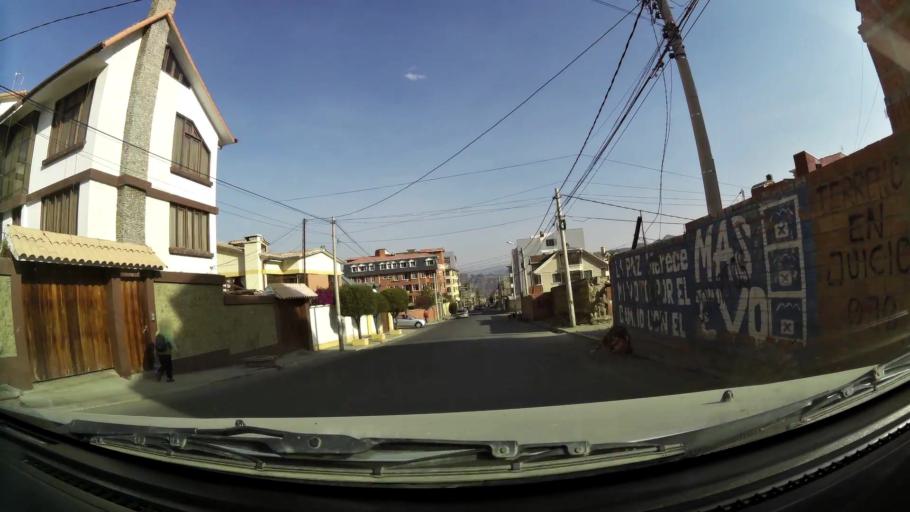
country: BO
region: La Paz
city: La Paz
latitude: -16.5140
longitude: -68.0875
